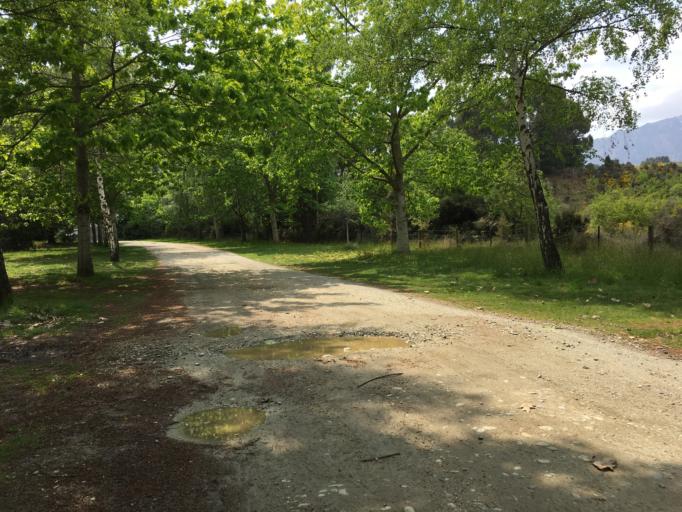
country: NZ
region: Otago
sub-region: Queenstown-Lakes District
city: Queenstown
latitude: -45.0467
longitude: 168.6905
